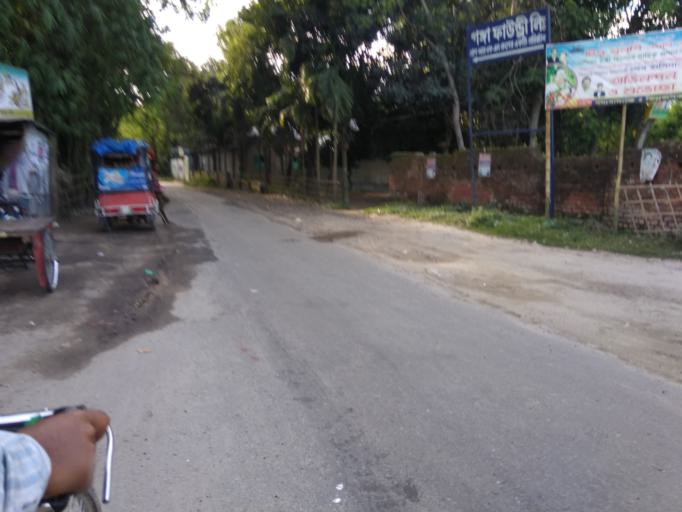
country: BD
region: Rangpur Division
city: Rangpur
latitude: 25.8299
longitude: 89.1197
